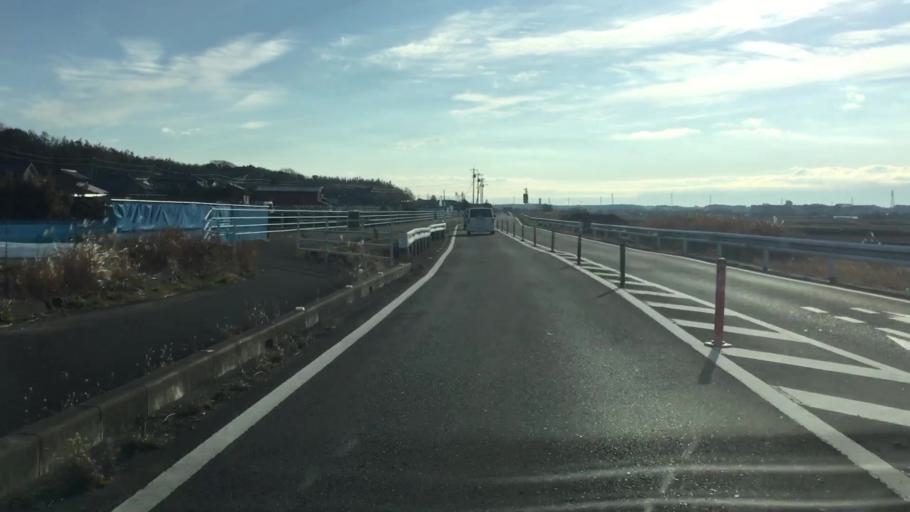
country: JP
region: Ibaraki
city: Toride
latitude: 35.8537
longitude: 140.1214
